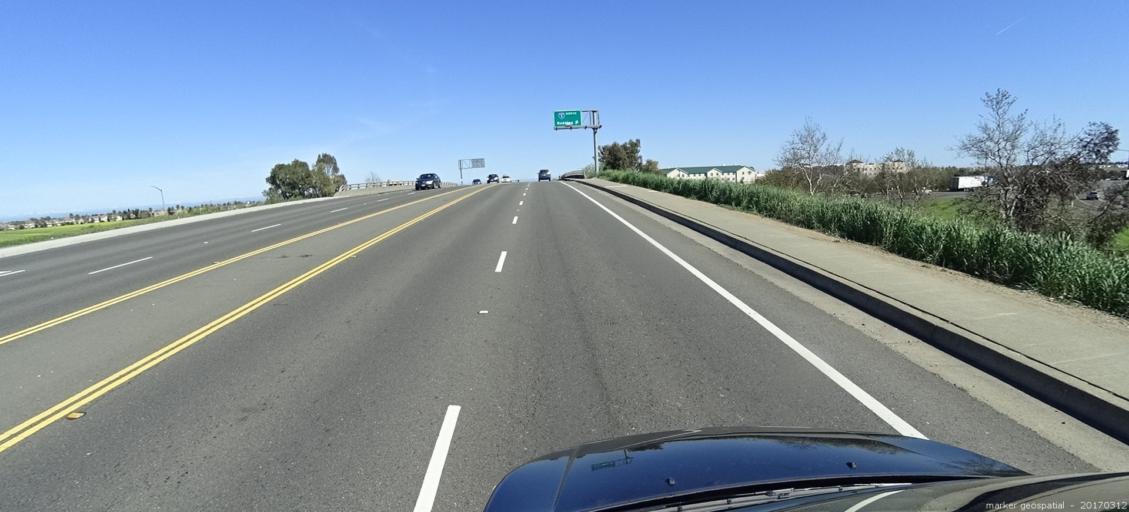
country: US
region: California
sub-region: Yolo County
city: West Sacramento
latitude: 38.6557
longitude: -121.5345
